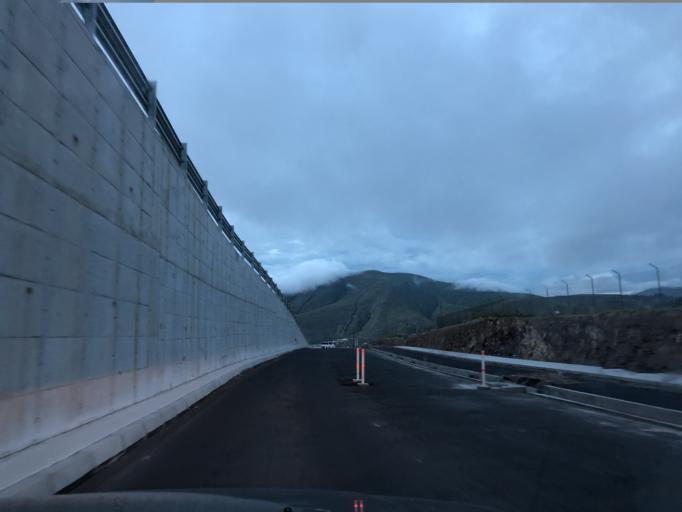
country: EC
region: Imbabura
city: Ibarra
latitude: 0.3739
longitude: -78.1278
